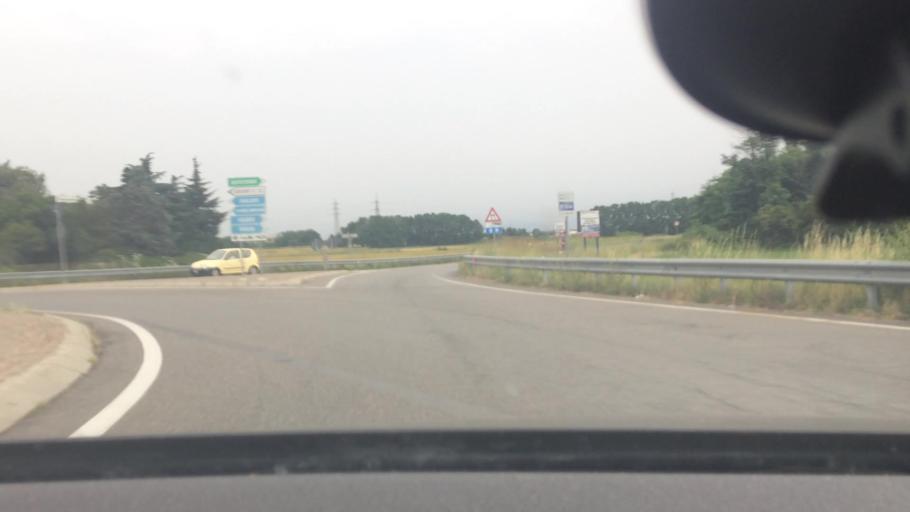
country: IT
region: Lombardy
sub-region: Provincia di Monza e Brianza
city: Ceriano Laghetto
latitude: 45.6292
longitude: 9.0600
